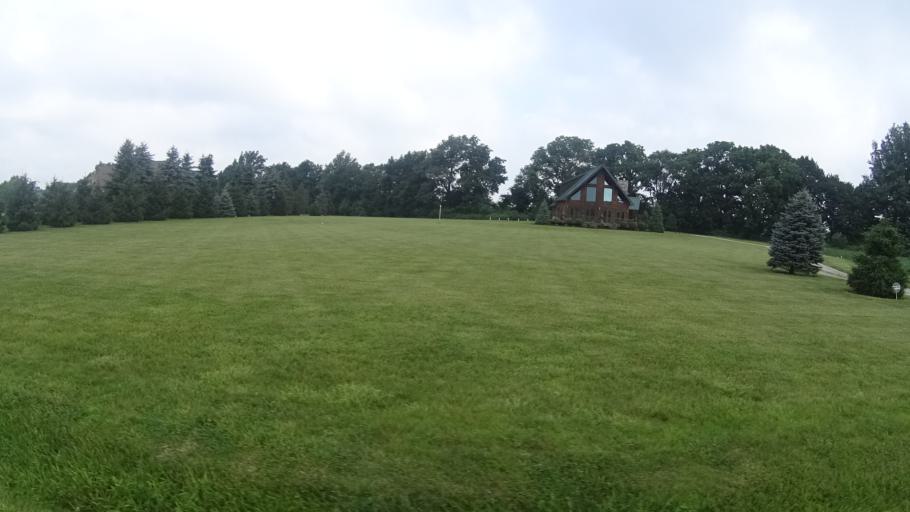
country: US
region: Ohio
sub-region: Huron County
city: Wakeman
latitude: 41.2996
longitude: -82.4974
